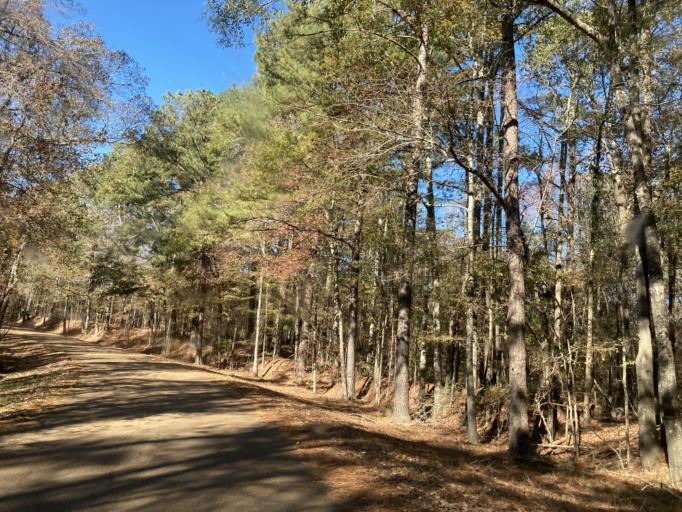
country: US
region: Mississippi
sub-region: Hinds County
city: Lynchburg
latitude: 32.5950
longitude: -90.5341
